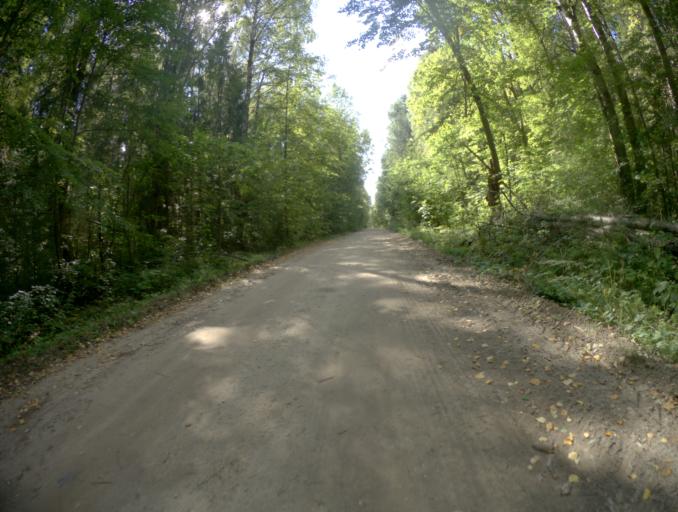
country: RU
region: Vladimir
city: Krasnaya Gorbatka
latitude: 55.8612
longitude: 41.8180
